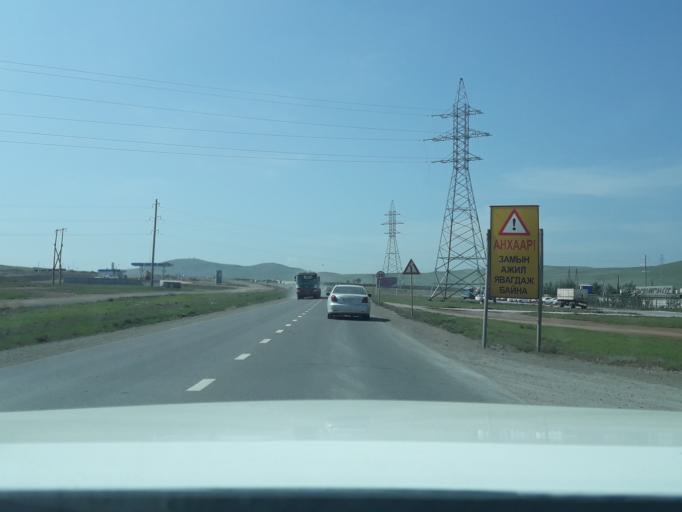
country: MN
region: Ulaanbaatar
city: Ulaanbaatar
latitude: 47.8194
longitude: 106.7595
